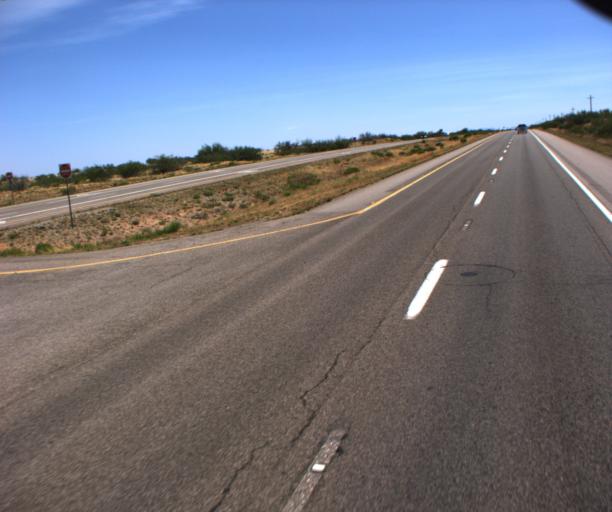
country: US
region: Arizona
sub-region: Cochise County
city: Whetstone
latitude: 31.9197
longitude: -110.3413
